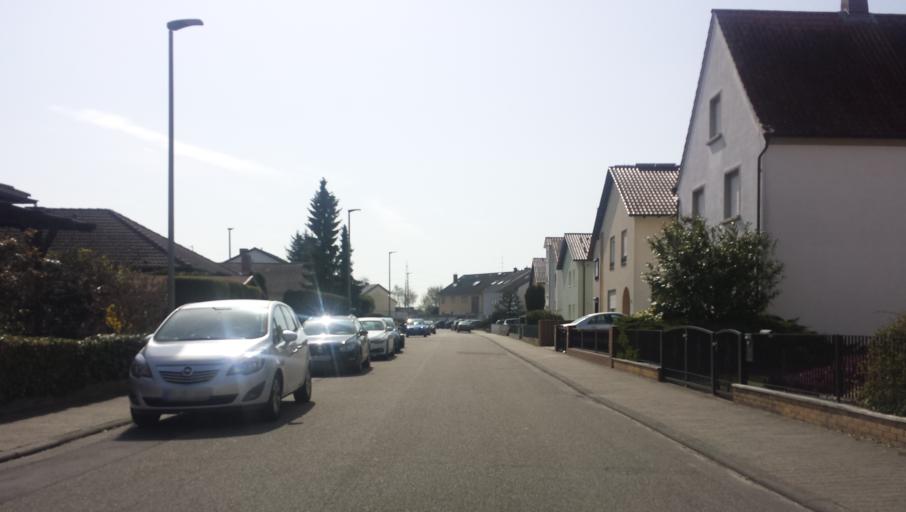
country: DE
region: Rheinland-Pfalz
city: Mutterstadt
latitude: 49.4361
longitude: 8.3620
